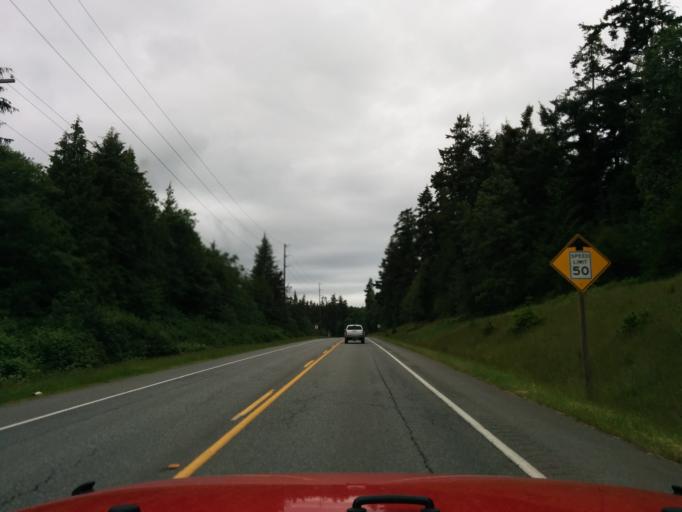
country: US
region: Washington
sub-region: Island County
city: Camano
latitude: 48.1675
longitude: -122.6075
